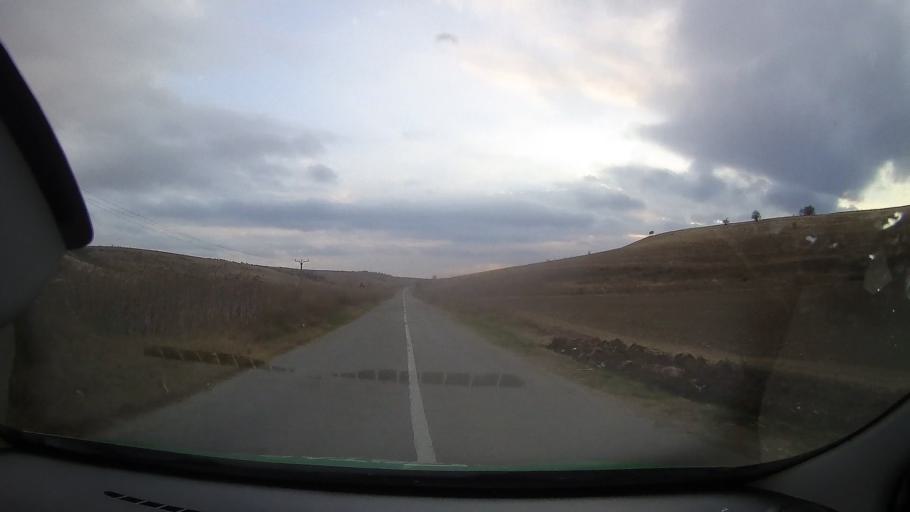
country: RO
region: Constanta
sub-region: Comuna Dobromir
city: Dobromir
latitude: 44.0346
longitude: 27.8023
